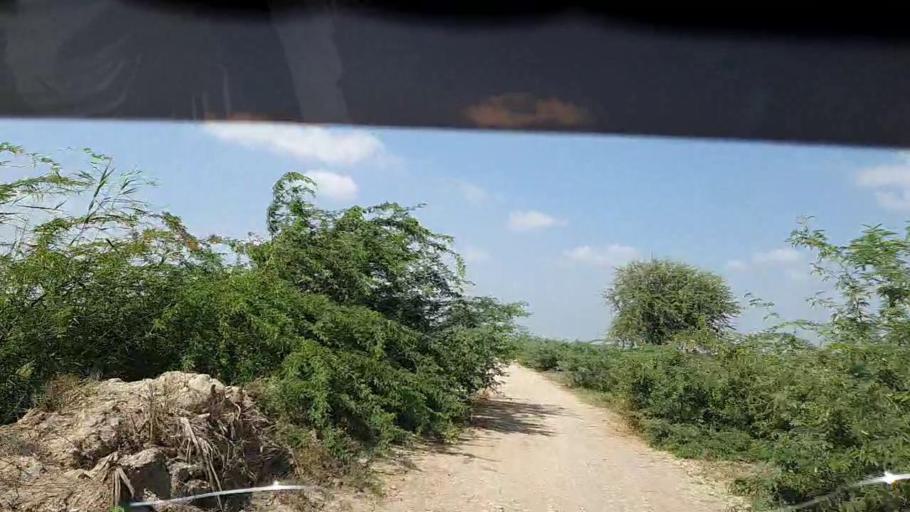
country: PK
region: Sindh
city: Kadhan
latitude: 24.5937
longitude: 69.0246
